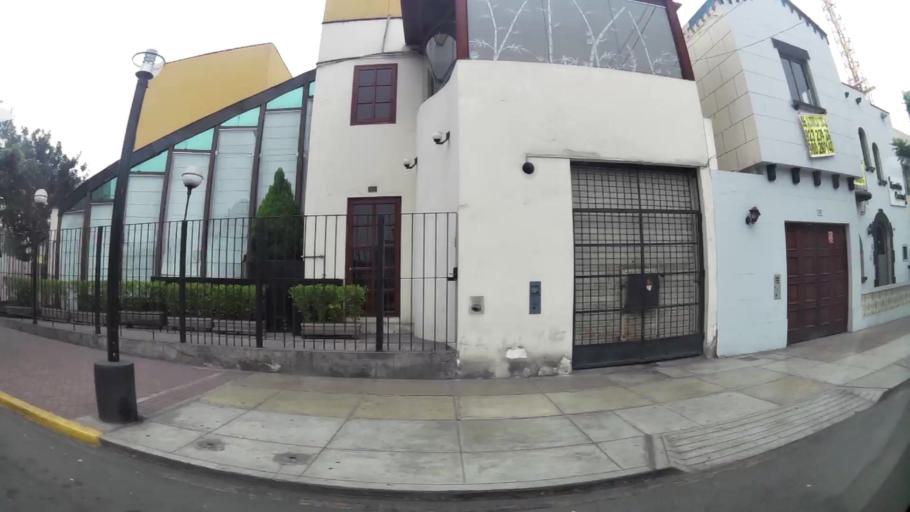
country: PE
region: Lima
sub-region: Lima
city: San Isidro
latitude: -12.1202
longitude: -77.0361
